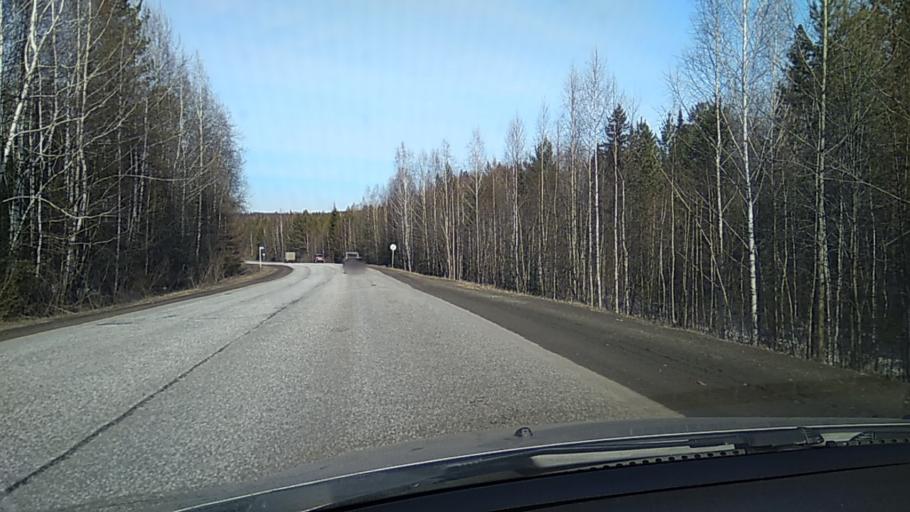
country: RU
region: Sverdlovsk
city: Chernoistochinsk
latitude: 57.7812
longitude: 59.8968
